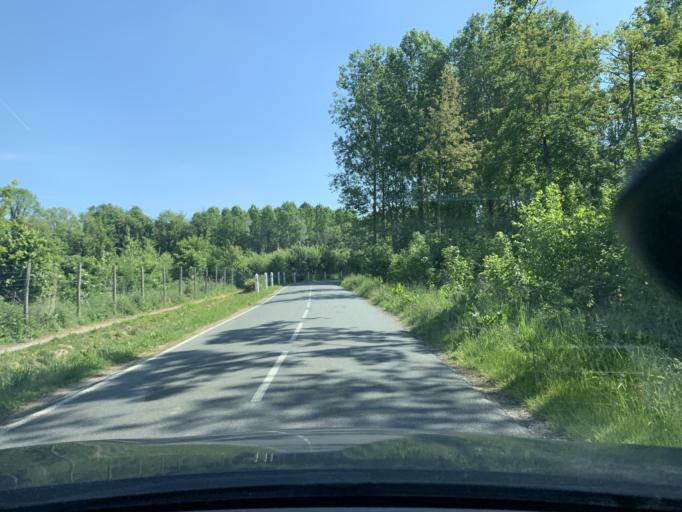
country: FR
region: Nord-Pas-de-Calais
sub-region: Departement du Nord
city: Fontaine-Notre-Dame
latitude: 50.1538
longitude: 3.1788
